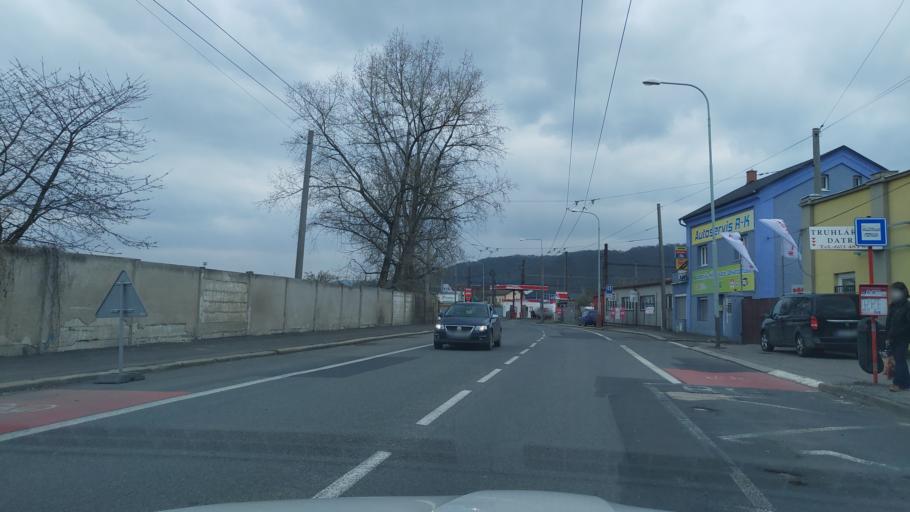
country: CZ
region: Ustecky
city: Trmice
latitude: 50.6566
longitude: 14.0088
